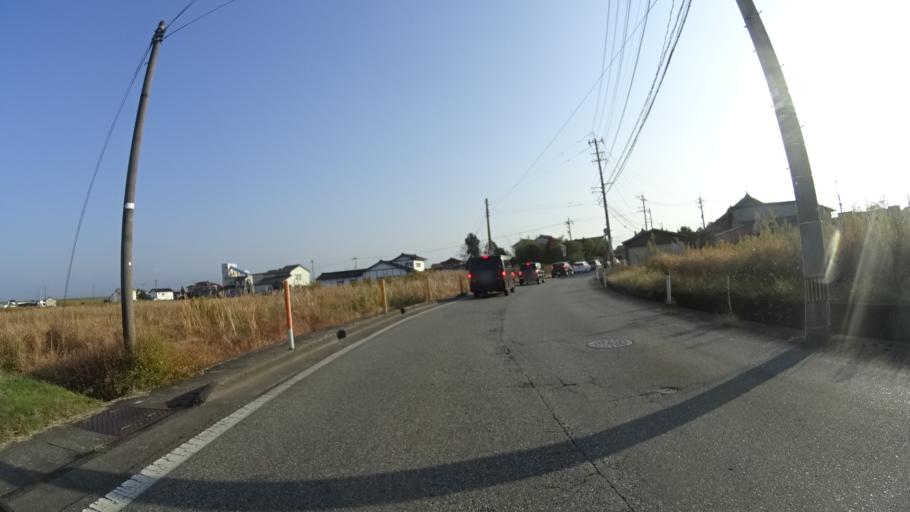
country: JP
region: Toyama
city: Toyama-shi
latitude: 36.6895
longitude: 137.2710
